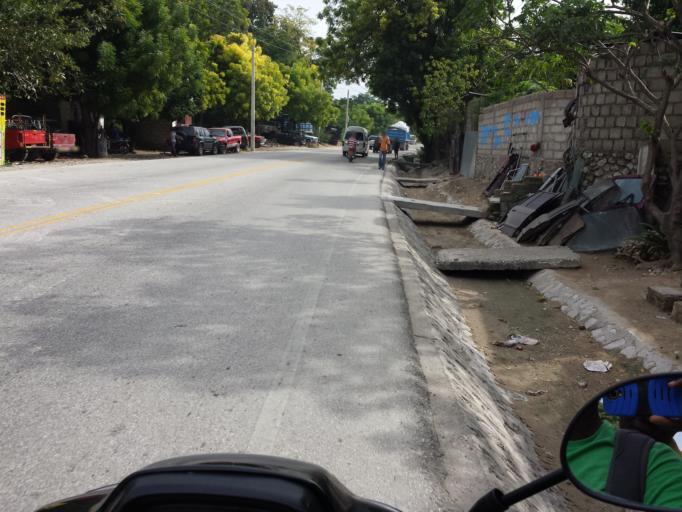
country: HT
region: Artibonite
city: Saint-Marc
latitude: 19.1270
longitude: -72.6914
